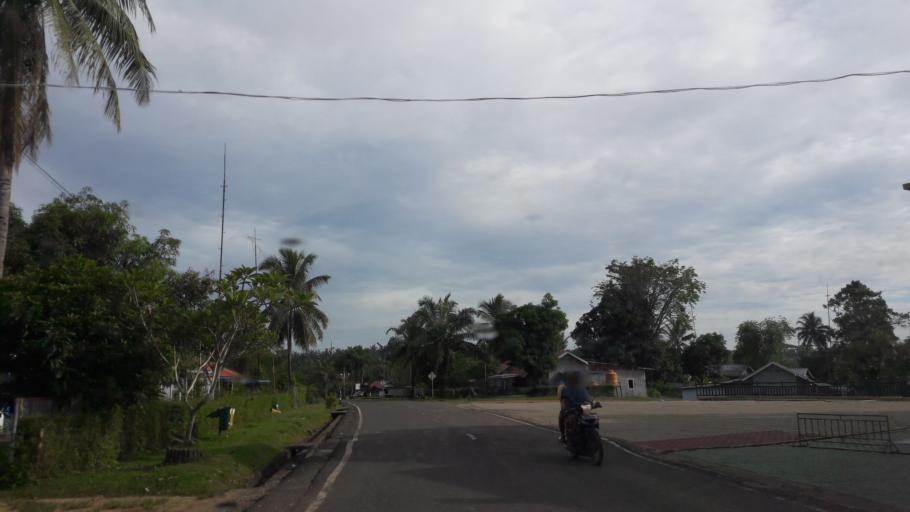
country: ID
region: South Sumatra
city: Gunungmegang Dalam
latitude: -3.2670
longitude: 103.8287
